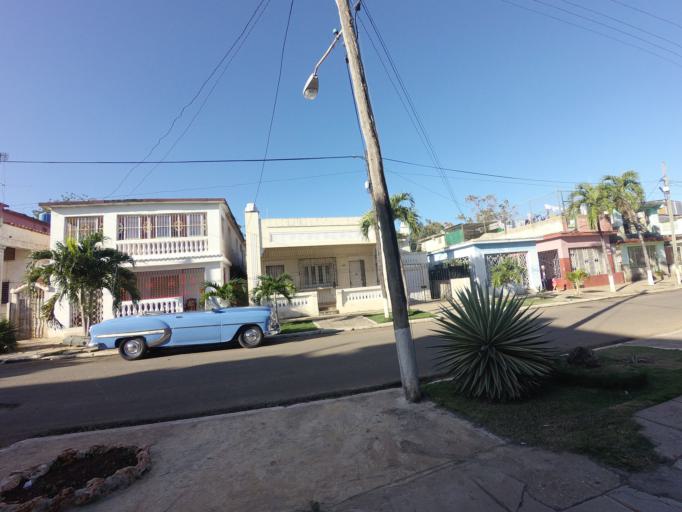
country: CU
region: La Habana
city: Cerro
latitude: 23.1008
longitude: -82.4302
